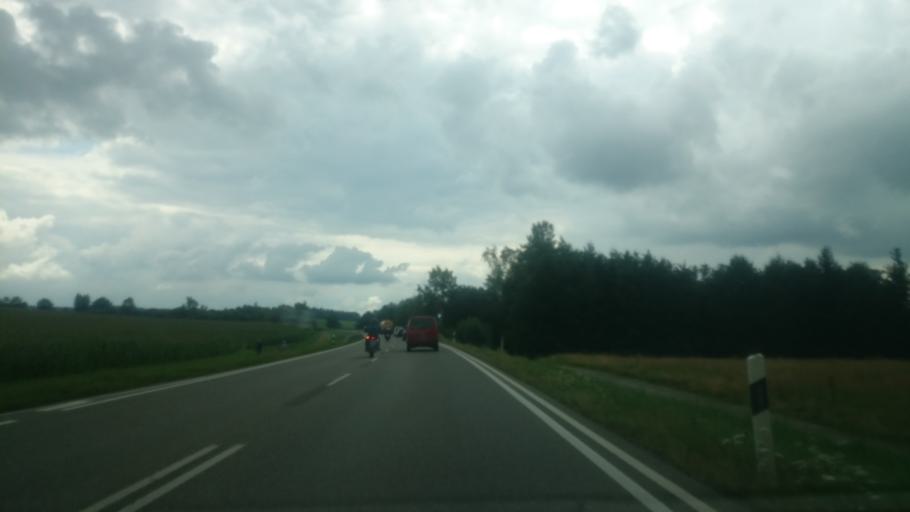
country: DE
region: Bavaria
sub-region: Swabia
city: Mauerstetten
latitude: 47.8767
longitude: 10.6453
